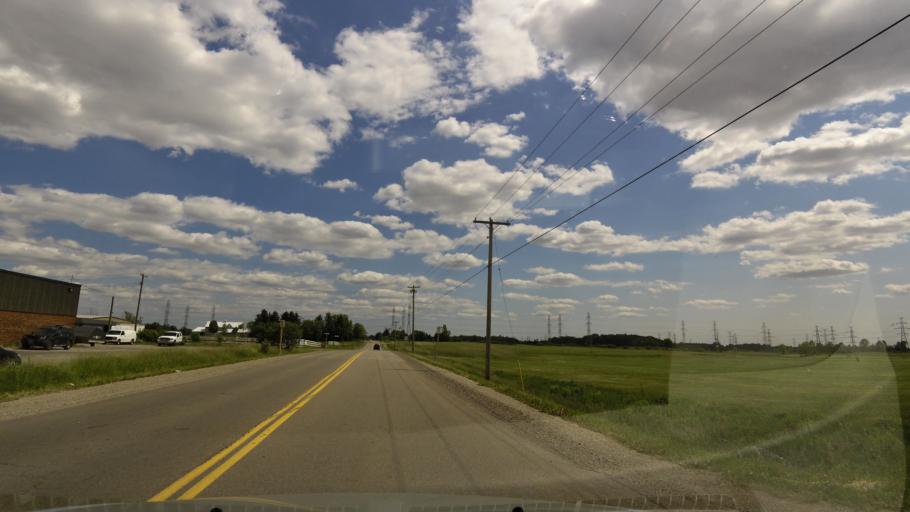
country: CA
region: Ontario
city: Ancaster
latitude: 43.1875
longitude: -80.0400
